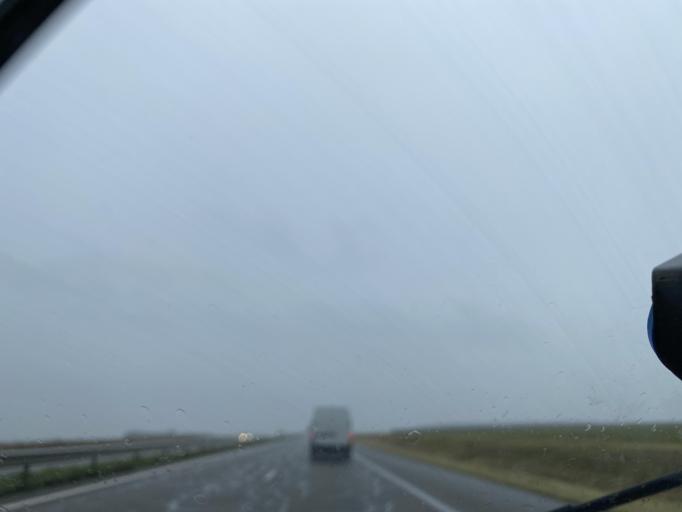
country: FR
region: Centre
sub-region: Departement d'Eure-et-Loir
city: Villemeux-sur-Eure
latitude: 48.6374
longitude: 1.4087
